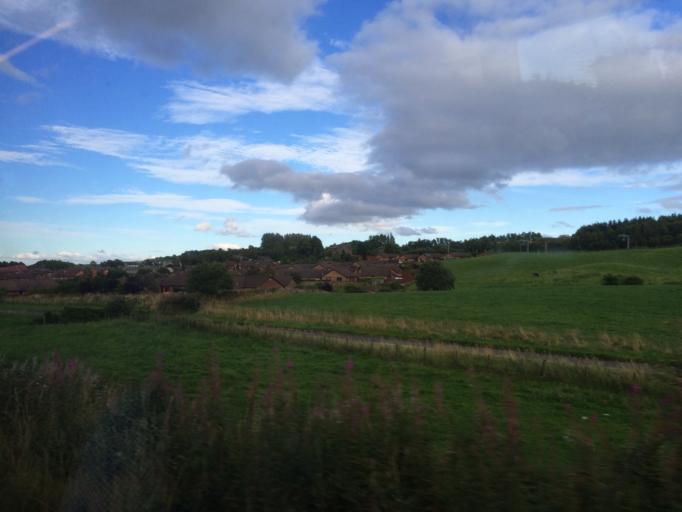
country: GB
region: Scotland
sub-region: Falkirk
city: Bonnybridge
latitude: 55.9925
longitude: -3.8844
